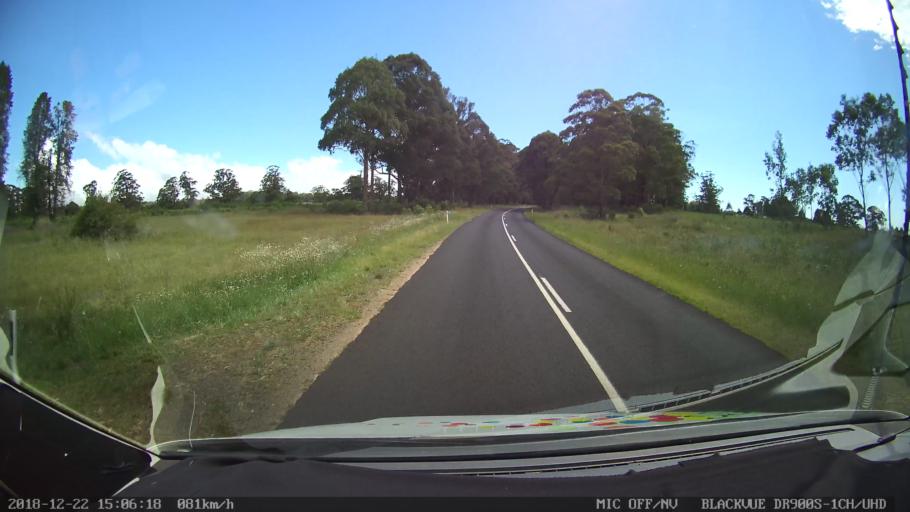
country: AU
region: New South Wales
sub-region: Bellingen
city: Dorrigo
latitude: -30.2923
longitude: 152.4287
